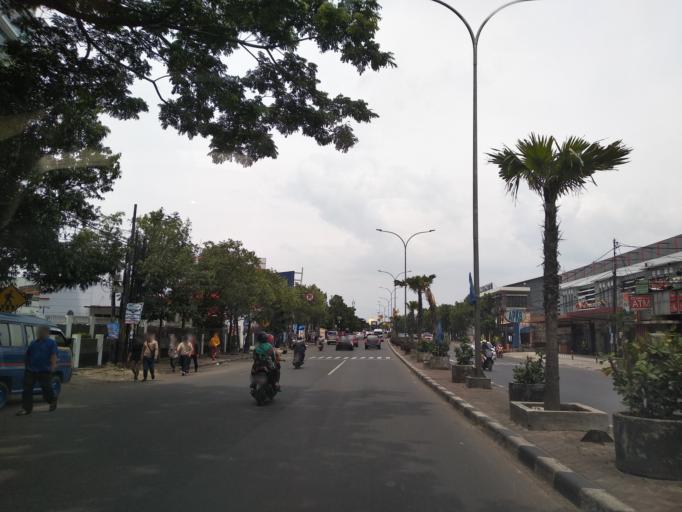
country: ID
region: West Java
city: Bandung
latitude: -6.9513
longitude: 107.6366
